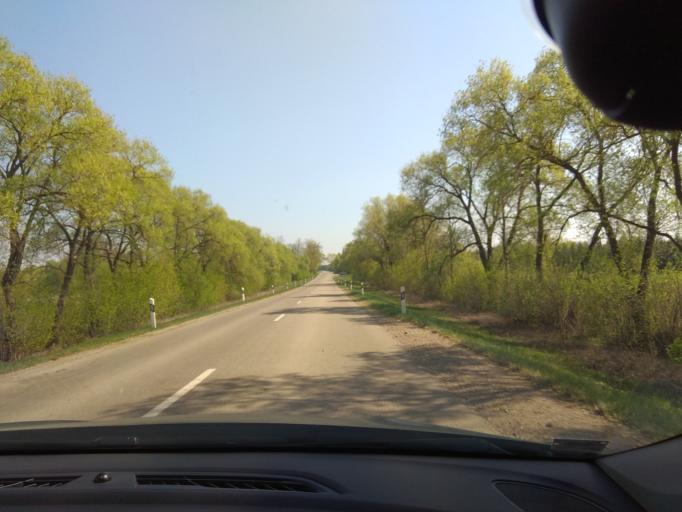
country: LT
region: Panevezys
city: Pasvalys
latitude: 55.9380
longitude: 24.2353
